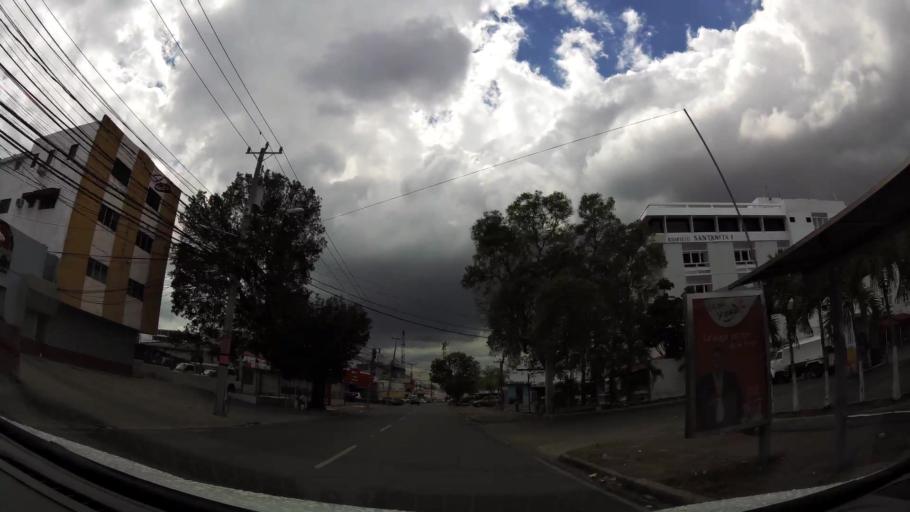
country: DO
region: Nacional
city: La Agustina
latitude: 18.4842
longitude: -69.9253
